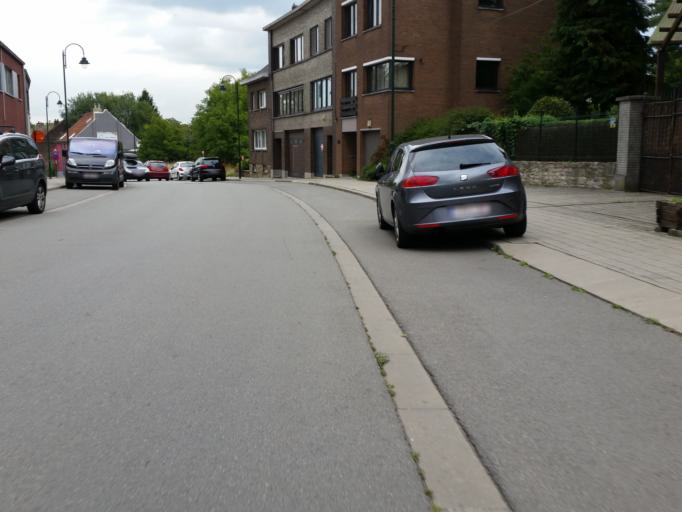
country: BE
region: Flanders
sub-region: Provincie Vlaams-Brabant
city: Diegem
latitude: 50.8966
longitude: 4.4216
